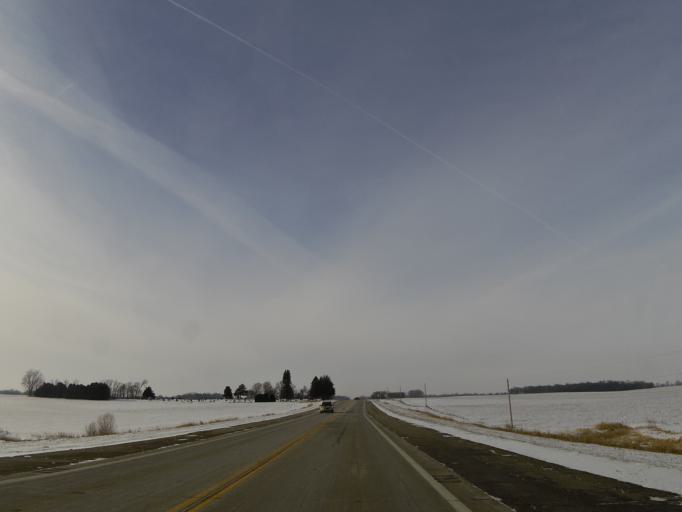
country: US
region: Minnesota
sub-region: McLeod County
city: Hutchinson
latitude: 44.8924
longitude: -94.2378
